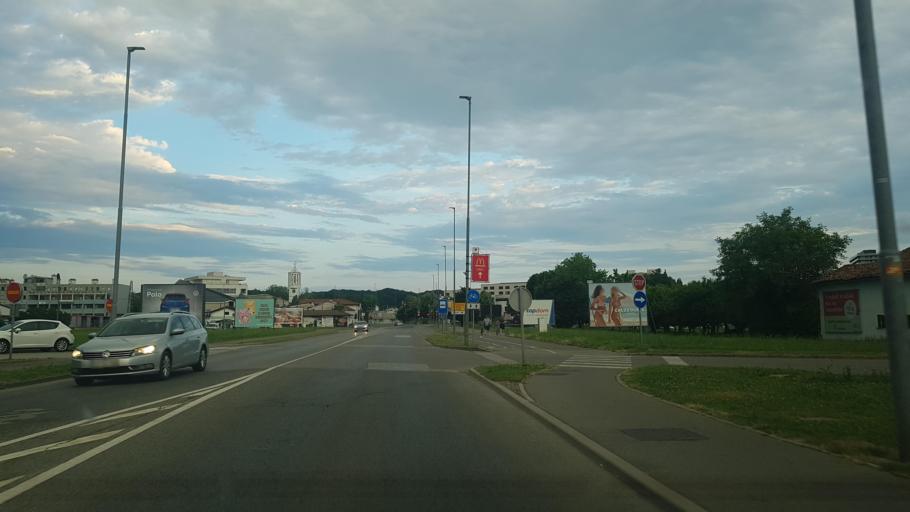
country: SI
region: Nova Gorica
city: Nova Gorica
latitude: 45.9623
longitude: 13.6493
